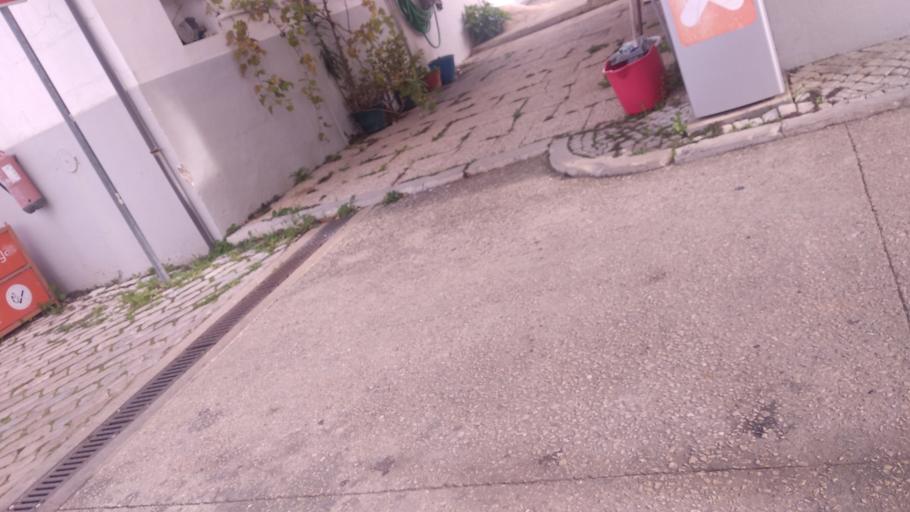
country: PT
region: Faro
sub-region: Sao Bras de Alportel
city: Sao Bras de Alportel
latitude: 37.1567
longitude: -7.8921
